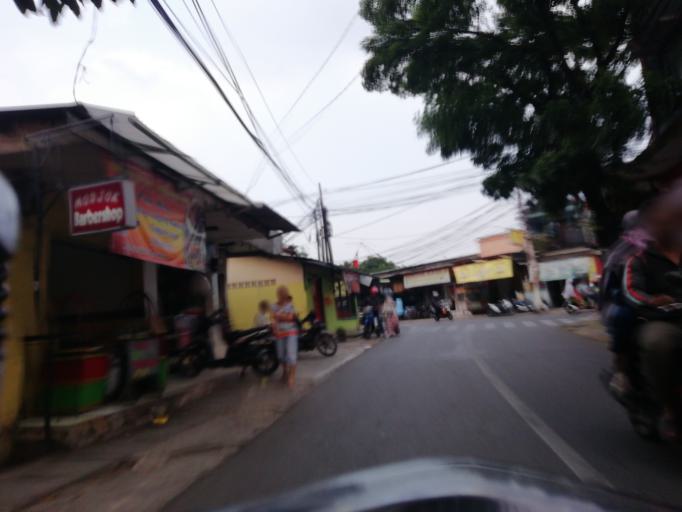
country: ID
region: West Java
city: Depok
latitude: -6.3360
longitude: 106.8254
